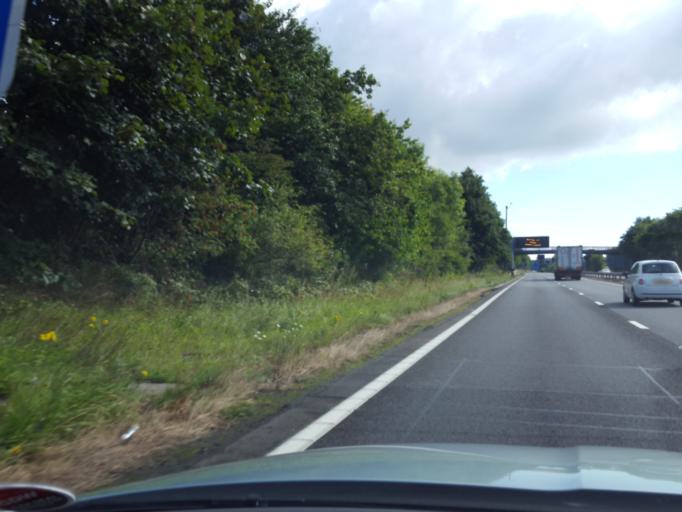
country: GB
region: Scotland
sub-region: Fife
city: Rosyth
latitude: 56.0466
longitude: -3.4209
